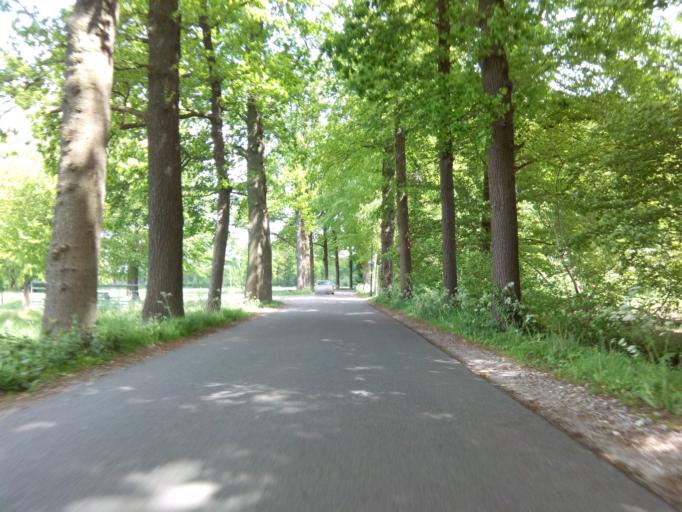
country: NL
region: Utrecht
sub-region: Gemeente Utrechtse Heuvelrug
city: Overberg
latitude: 52.0699
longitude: 5.4728
